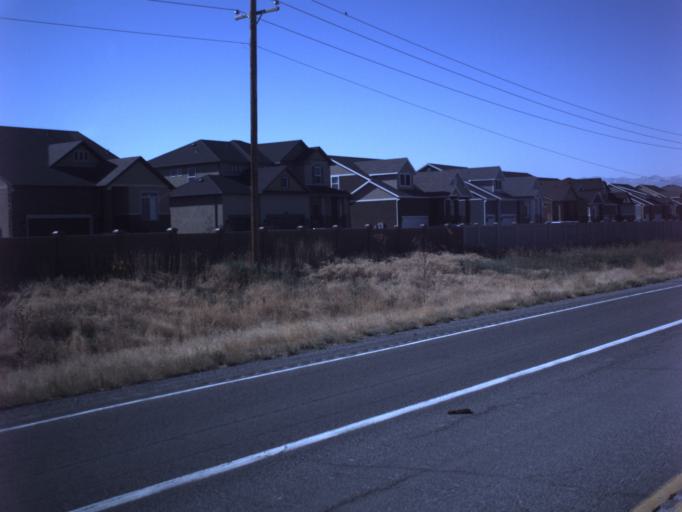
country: US
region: Utah
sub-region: Tooele County
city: Stansbury park
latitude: 40.6439
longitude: -112.3108
